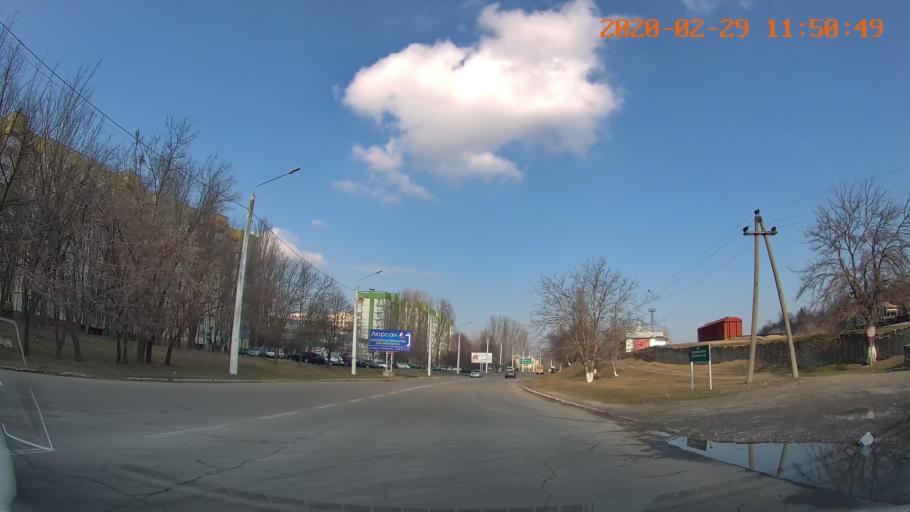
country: MD
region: Telenesti
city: Ribnita
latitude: 47.7612
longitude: 28.9897
